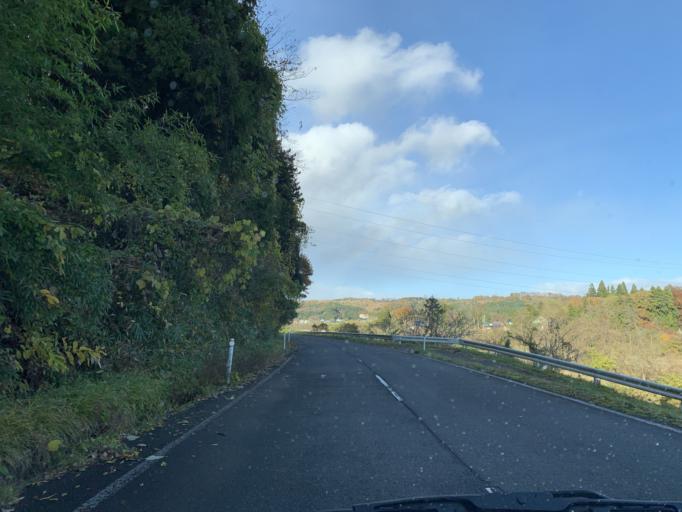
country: JP
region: Iwate
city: Ichinoseki
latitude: 39.0200
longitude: 141.0743
